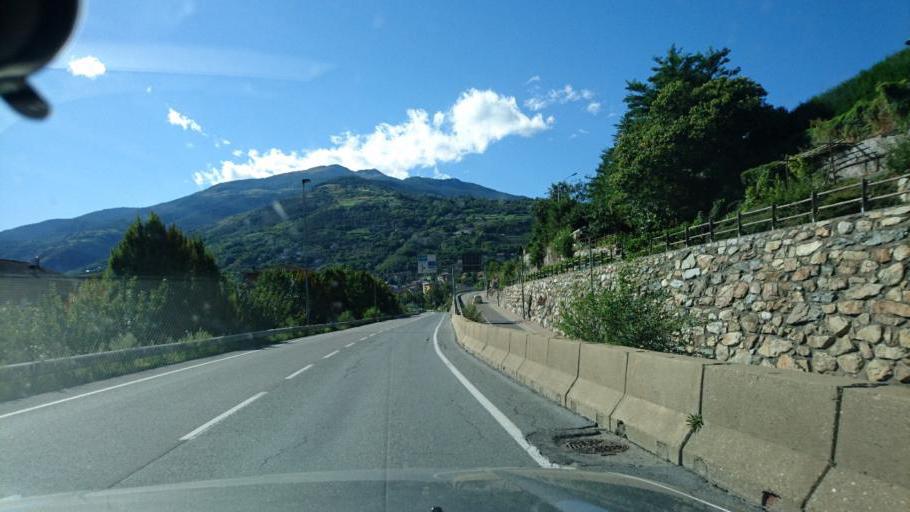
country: IT
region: Aosta Valley
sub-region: Valle d'Aosta
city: Aosta
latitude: 45.7413
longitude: 7.3292
